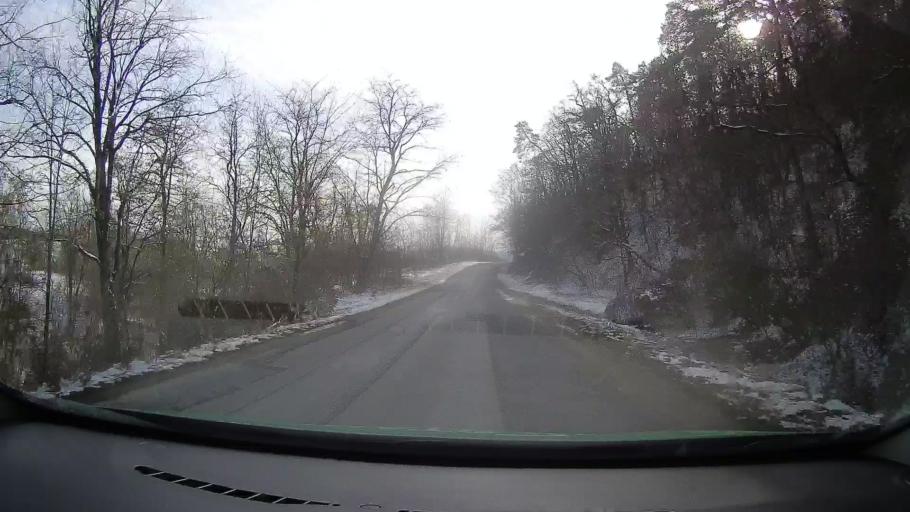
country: RO
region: Mures
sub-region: Comuna Apold
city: Saes
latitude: 46.1886
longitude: 24.7636
